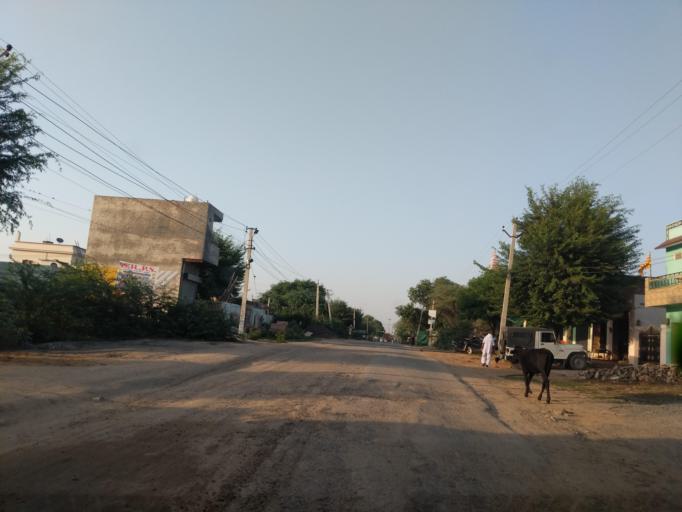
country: IN
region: Rajasthan
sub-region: Churu
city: Rajgarh
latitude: 28.6231
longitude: 75.3796
